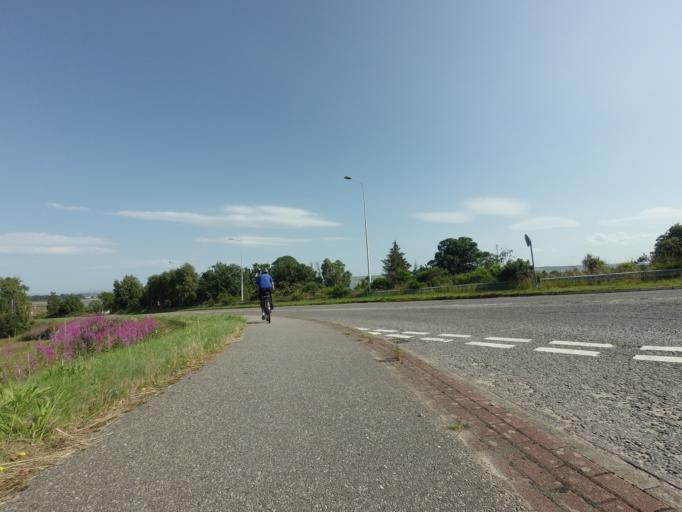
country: GB
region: Scotland
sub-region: Highland
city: Alness
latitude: 57.6837
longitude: -4.2950
